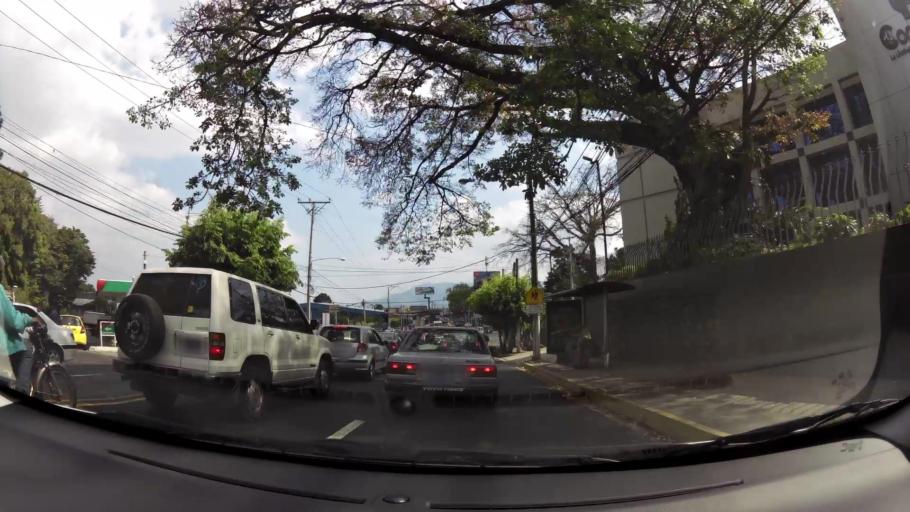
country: SV
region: San Salvador
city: Mejicanos
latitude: 13.7079
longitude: -89.2277
